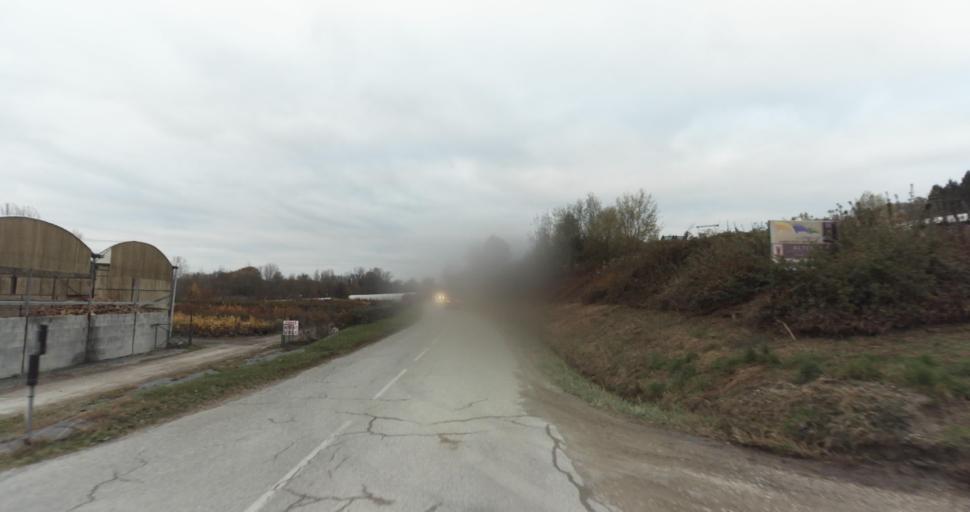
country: FR
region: Rhone-Alpes
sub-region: Departement de la Haute-Savoie
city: Saint-Felix
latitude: 45.7866
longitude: 5.9678
